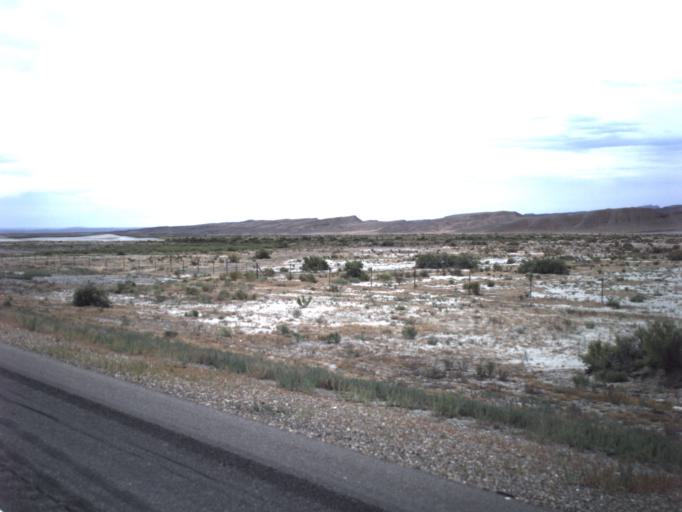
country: US
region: Utah
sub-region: Carbon County
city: East Carbon City
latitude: 39.1255
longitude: -110.3335
